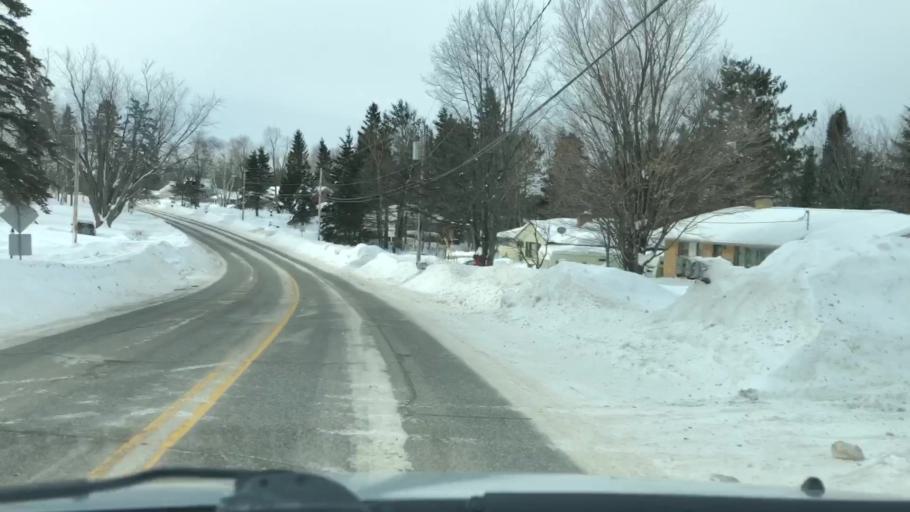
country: US
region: Minnesota
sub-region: Saint Louis County
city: Duluth
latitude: 46.7975
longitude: -92.1490
